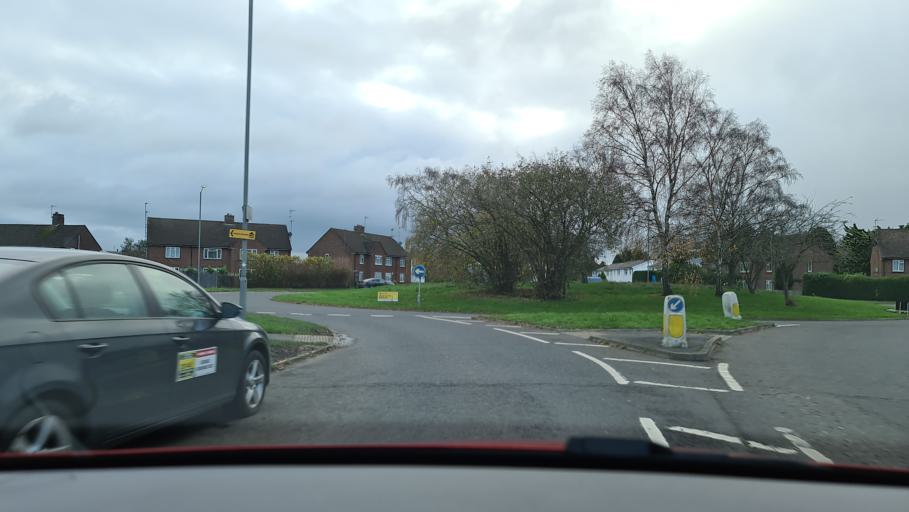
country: GB
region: England
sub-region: Buckinghamshire
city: Aylesbury
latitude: 51.8106
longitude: -0.8246
